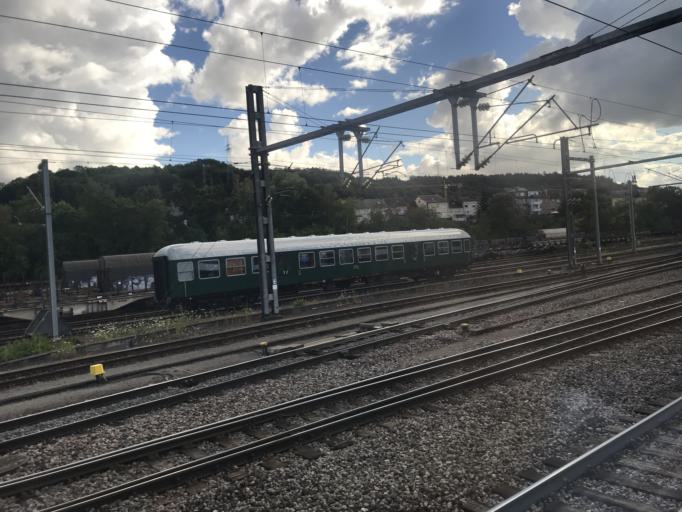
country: LU
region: Luxembourg
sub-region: Canton d'Esch-sur-Alzette
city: Petange
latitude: 49.5549
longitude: 5.8841
